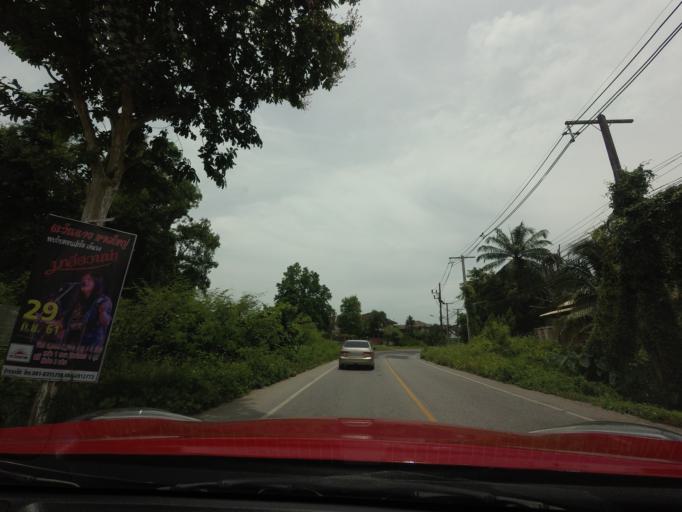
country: TH
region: Songkhla
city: Na Mom
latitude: 7.0023
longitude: 100.5300
